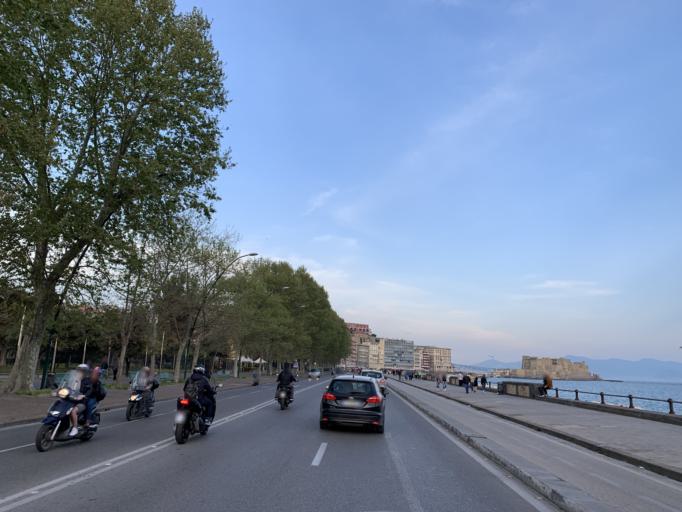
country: IT
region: Campania
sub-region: Provincia di Napoli
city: Napoli
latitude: 40.8320
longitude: 14.2366
